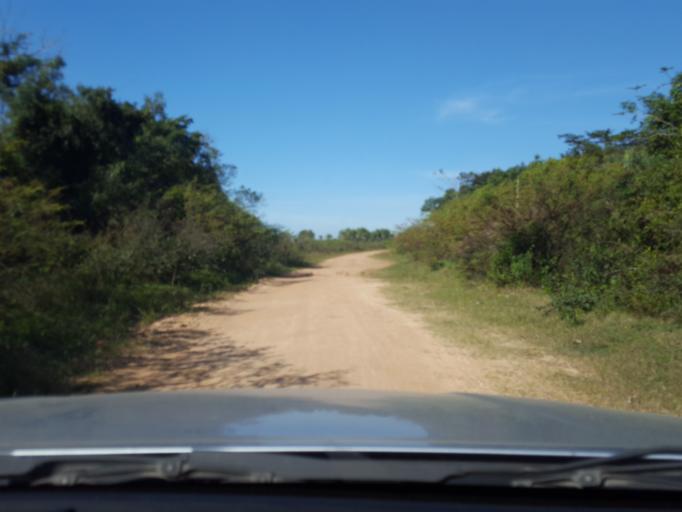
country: PY
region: Cordillera
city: Atyra
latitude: -25.2497
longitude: -57.1190
